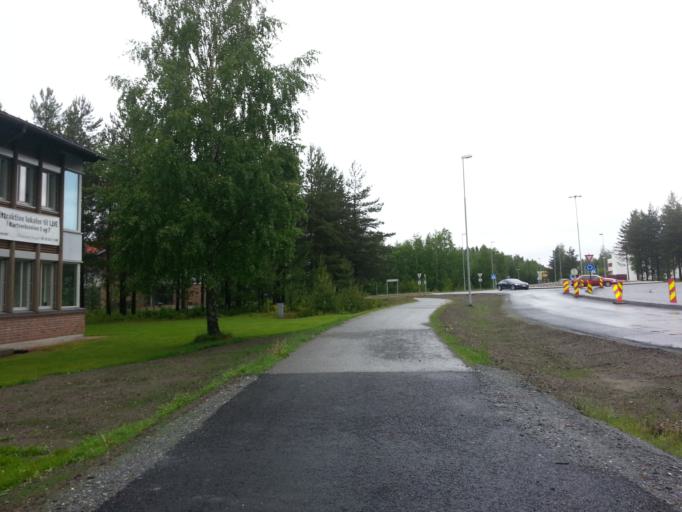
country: NO
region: Buskerud
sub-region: Ringerike
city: Honefoss
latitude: 60.1459
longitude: 10.2494
